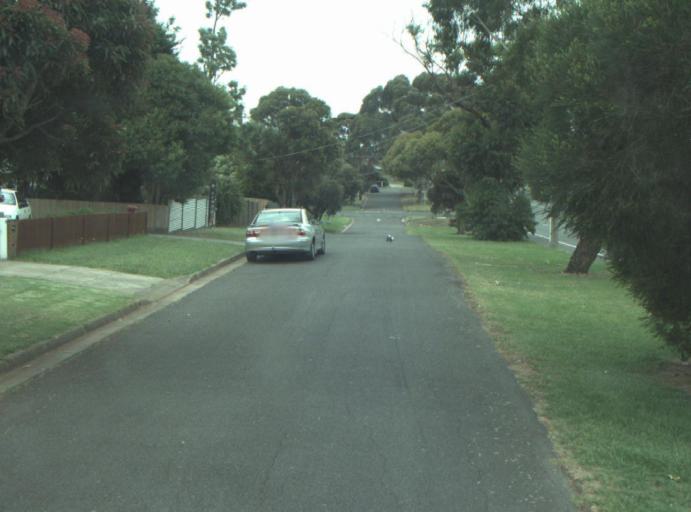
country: AU
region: Victoria
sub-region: Greater Geelong
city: Breakwater
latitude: -38.1868
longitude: 144.3438
